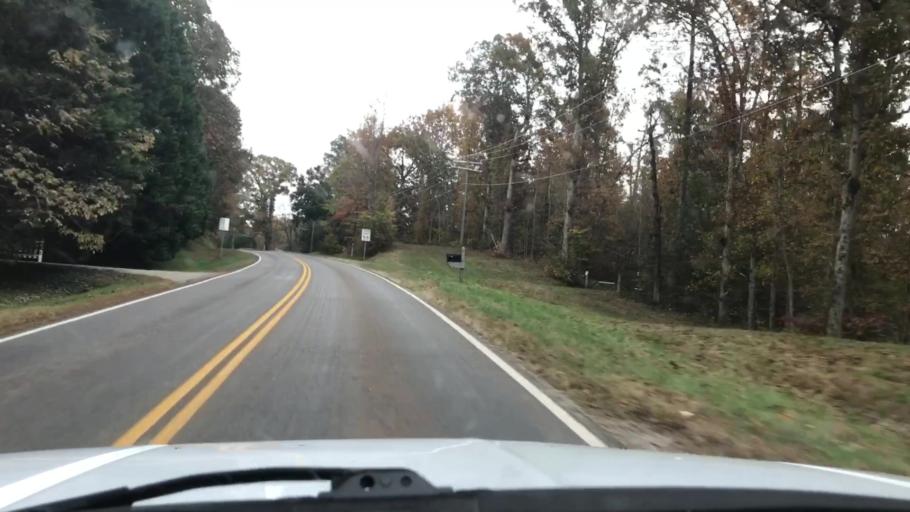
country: US
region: Virginia
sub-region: Goochland County
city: Goochland
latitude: 37.6668
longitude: -77.8792
